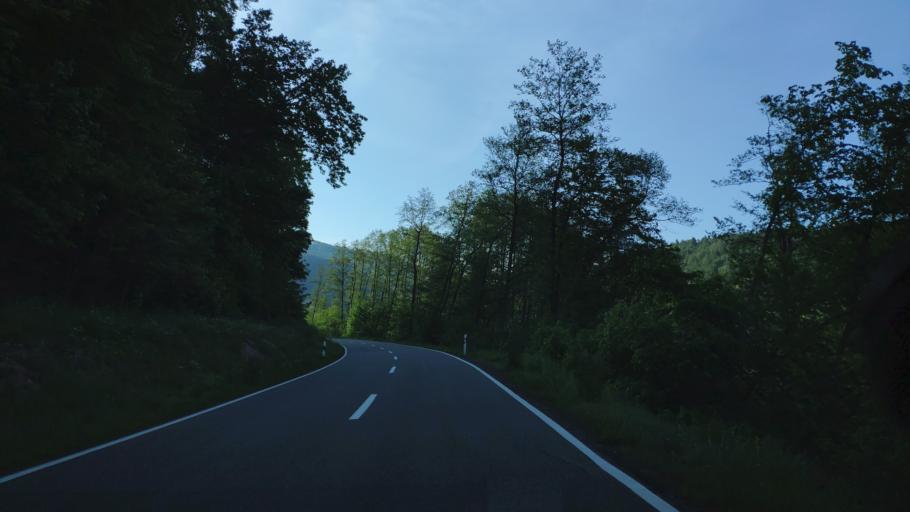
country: DE
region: Rheinland-Pfalz
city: Fischbach
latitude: 49.0806
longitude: 7.7363
